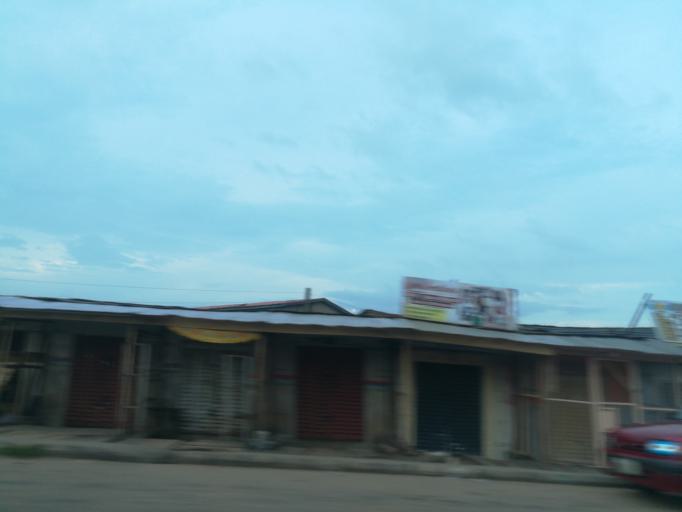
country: NG
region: Oyo
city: Ibadan
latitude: 7.4244
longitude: 3.8993
